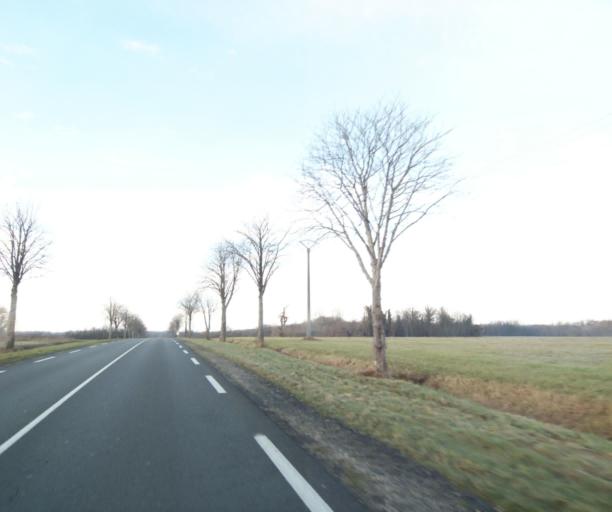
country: FR
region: Poitou-Charentes
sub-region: Departement de la Charente-Maritime
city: Fontcouverte
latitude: 45.8065
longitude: -0.5571
